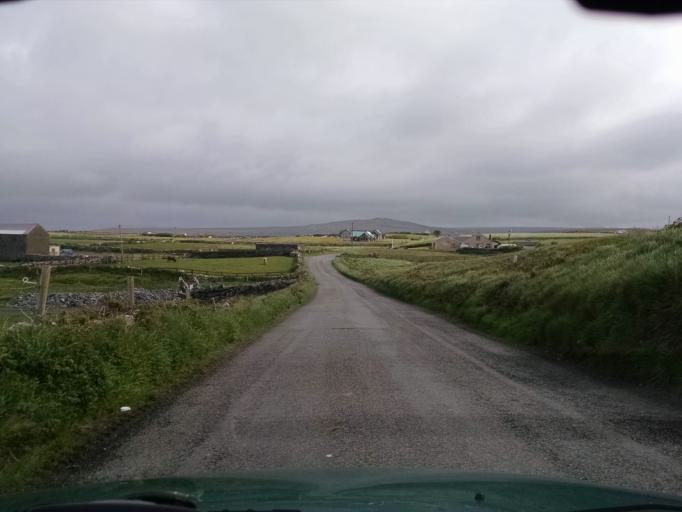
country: IE
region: Connaught
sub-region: County Galway
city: Bearna
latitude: 53.0324
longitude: -9.3647
